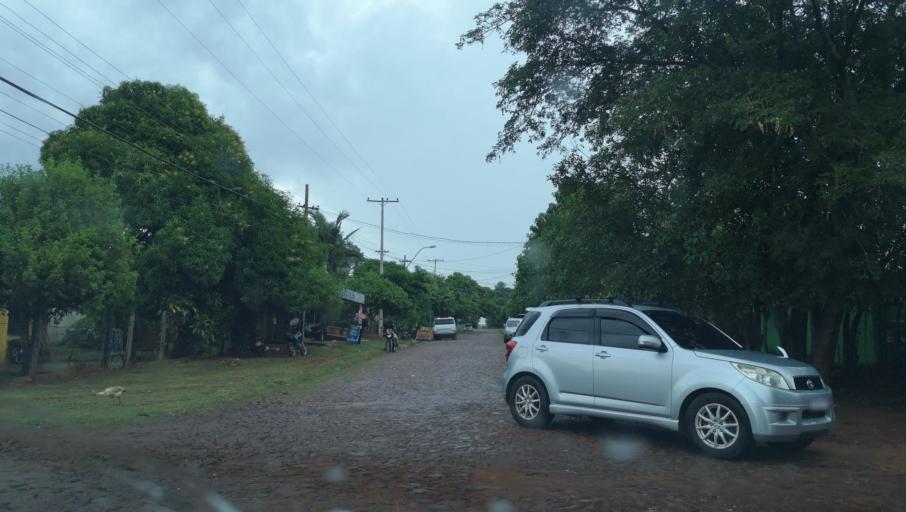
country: PY
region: Misiones
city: Santa Maria
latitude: -26.8951
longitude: -57.0256
